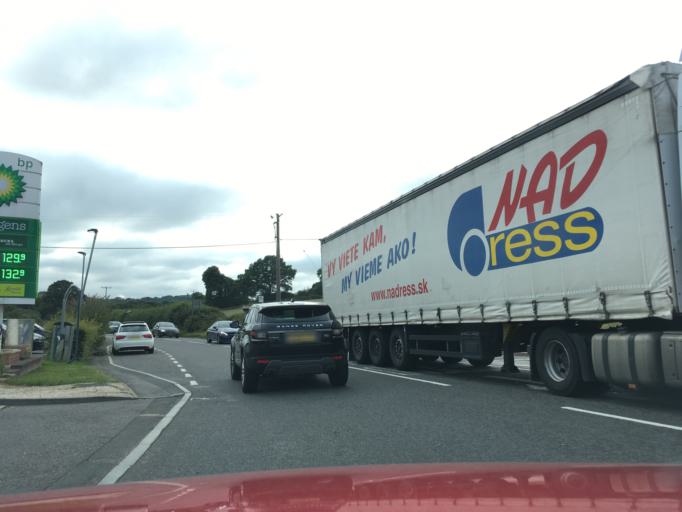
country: GB
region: England
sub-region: Hampshire
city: Four Marks
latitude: 51.0313
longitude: -1.0753
